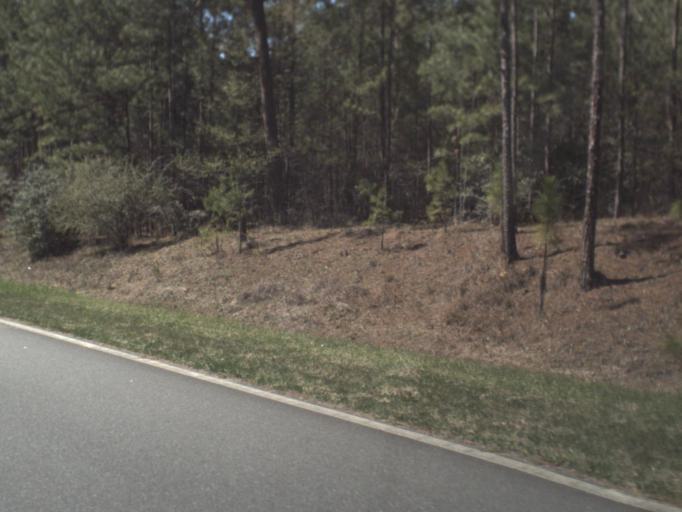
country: US
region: Florida
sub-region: Gadsden County
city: Chattahoochee
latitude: 30.7017
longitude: -84.8198
